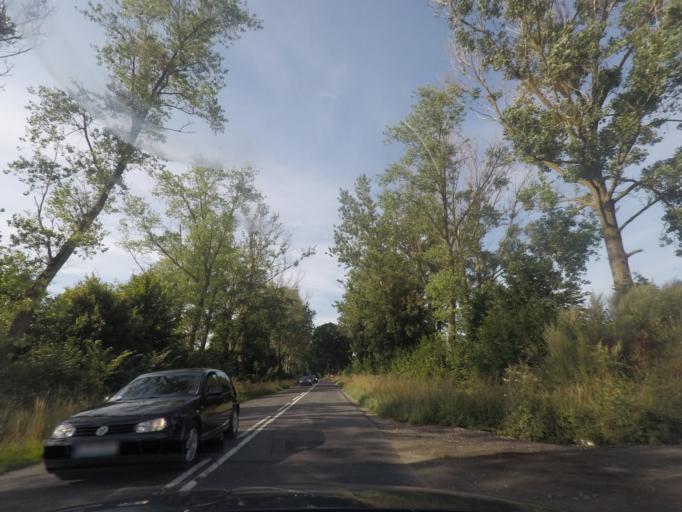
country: PL
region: Pomeranian Voivodeship
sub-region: Powiat leborski
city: Leba
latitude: 54.6872
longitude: 17.5960
